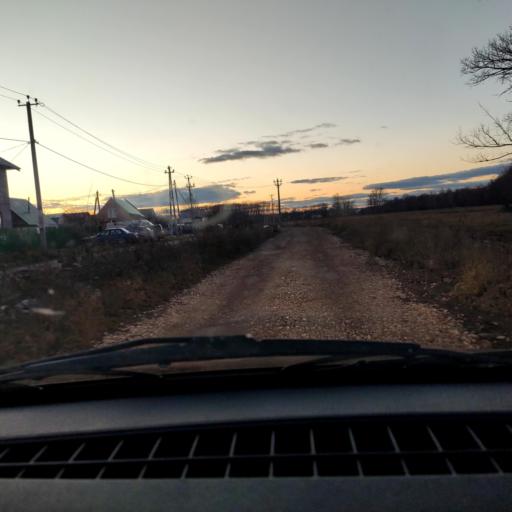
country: RU
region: Bashkortostan
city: Ufa
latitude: 54.6459
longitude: 55.9086
